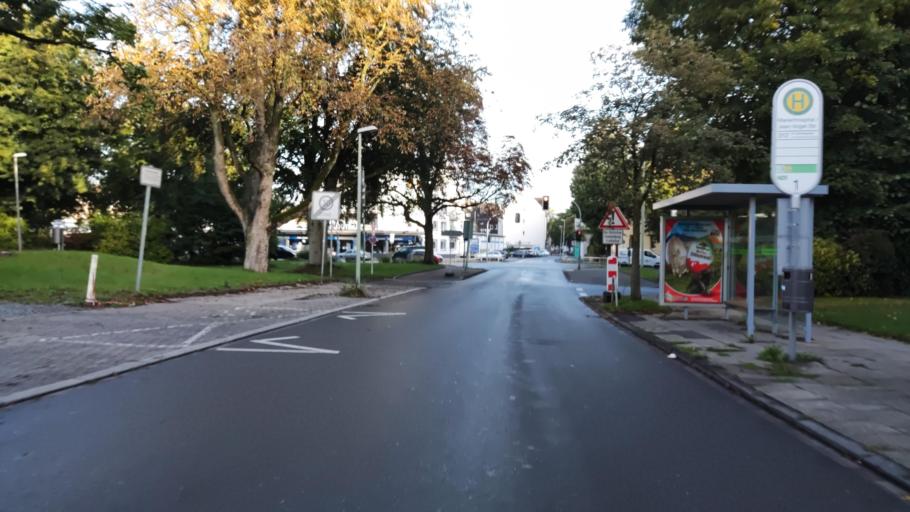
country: DE
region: North Rhine-Westphalia
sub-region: Regierungsbezirk Arnsberg
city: Herne
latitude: 51.5289
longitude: 7.2240
